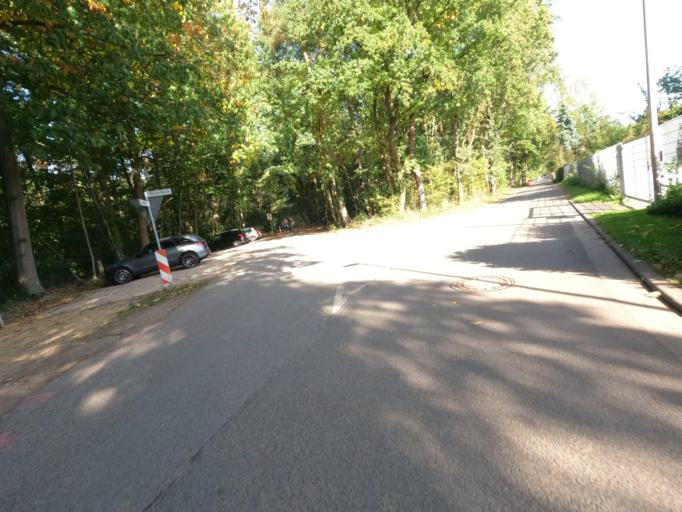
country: DE
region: North Rhine-Westphalia
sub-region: Regierungsbezirk Koln
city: Wassenberg
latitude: 51.1213
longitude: 6.1652
